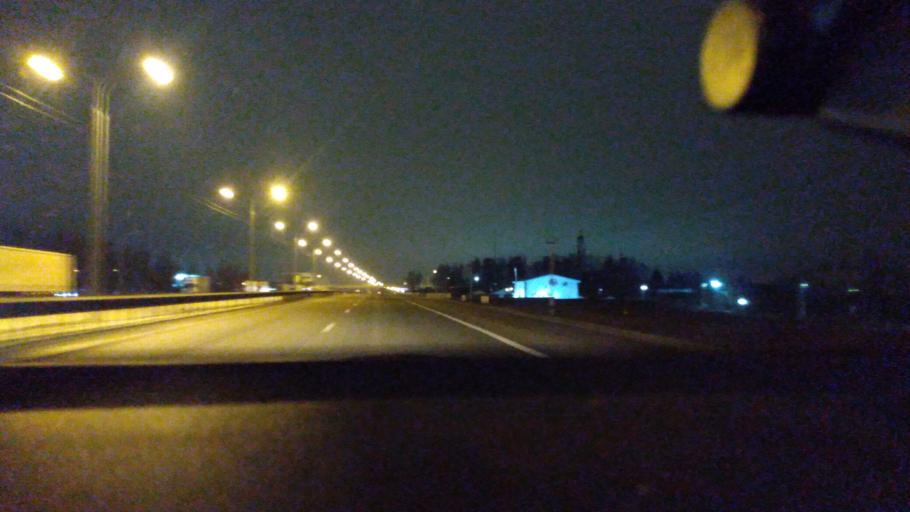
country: RU
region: Moskovskaya
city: Zhukovskiy
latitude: 55.5419
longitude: 38.0851
